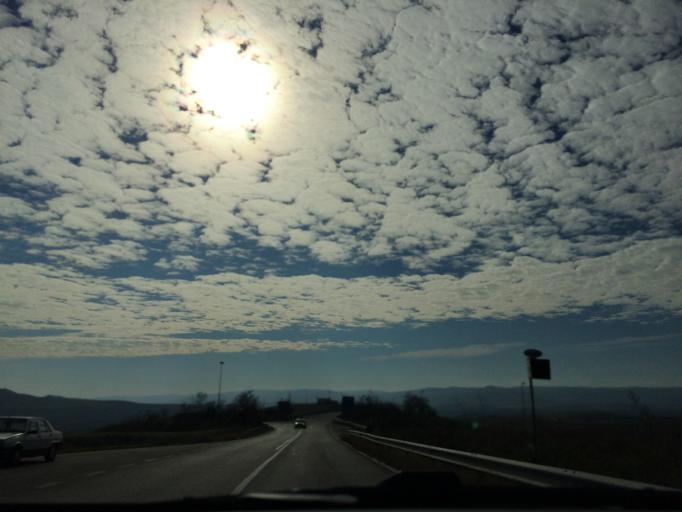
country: IT
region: Basilicate
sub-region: Provincia di Matera
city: Matera
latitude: 40.6474
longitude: 16.5938
